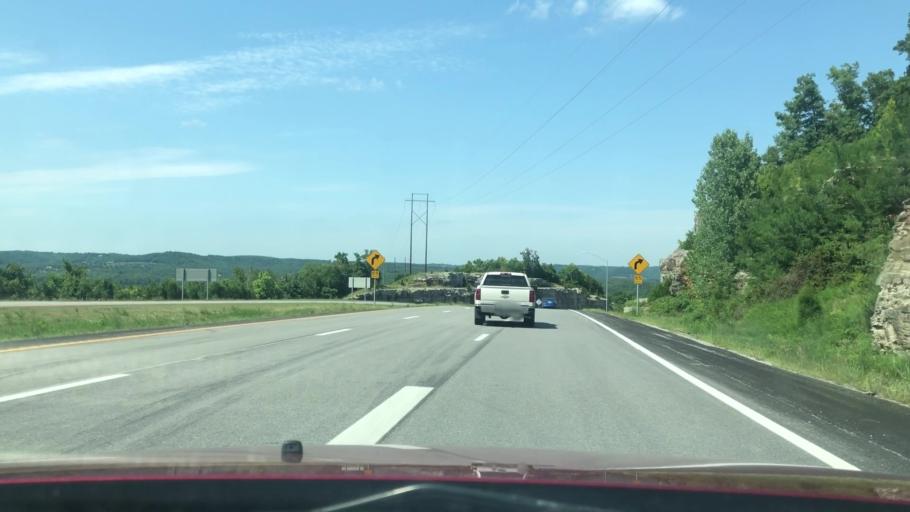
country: US
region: Missouri
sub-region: Taney County
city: Branson
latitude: 36.6795
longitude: -93.3161
